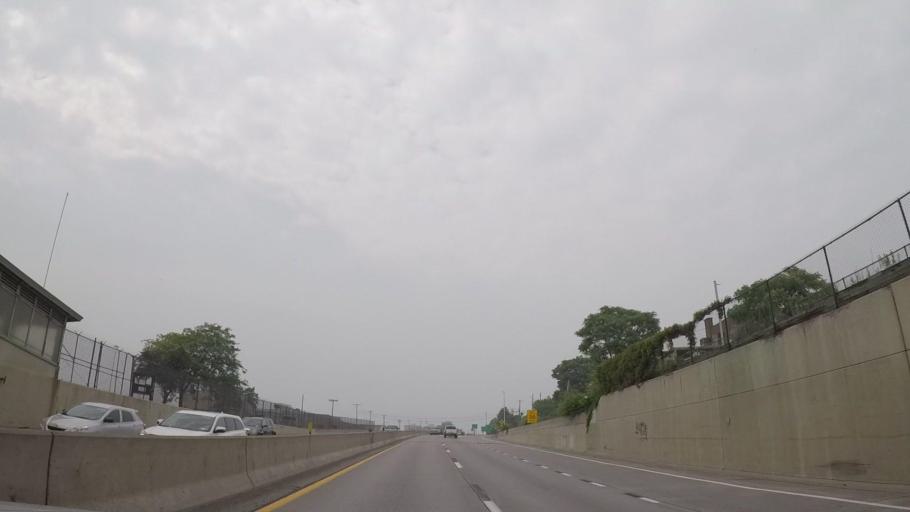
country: CA
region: Ontario
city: Fort Erie
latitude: 42.9327
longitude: -78.9021
